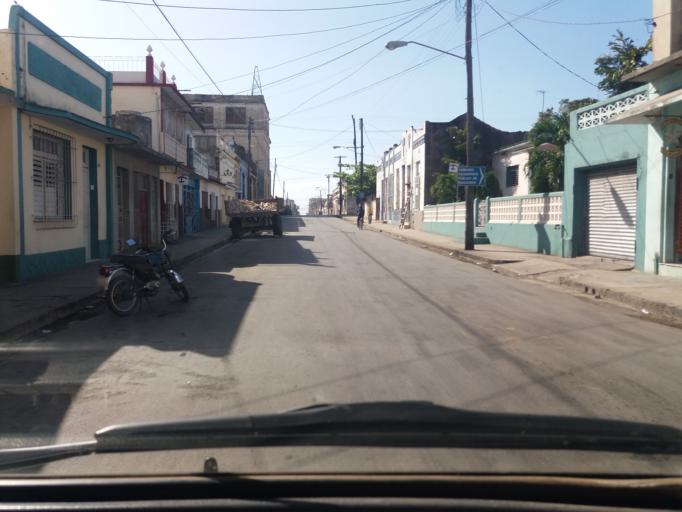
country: CU
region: Cienfuegos
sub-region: Municipio de Cienfuegos
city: Cienfuegos
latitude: 22.1454
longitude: -80.4427
